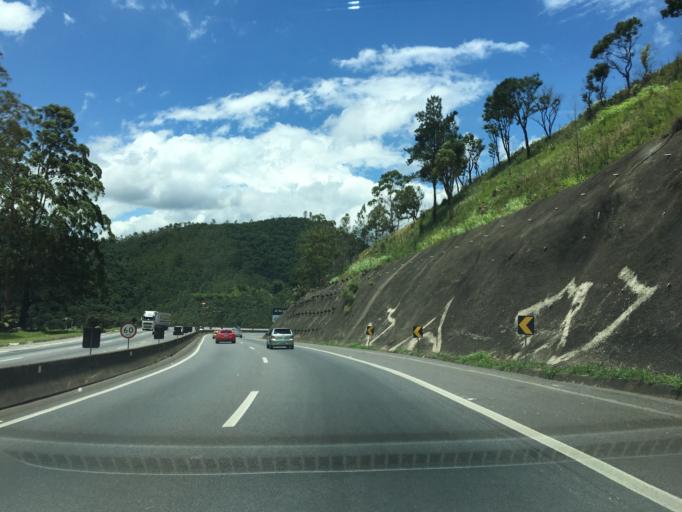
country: BR
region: Sao Paulo
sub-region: Mairipora
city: Mairipora
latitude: -23.2908
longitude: -46.5845
